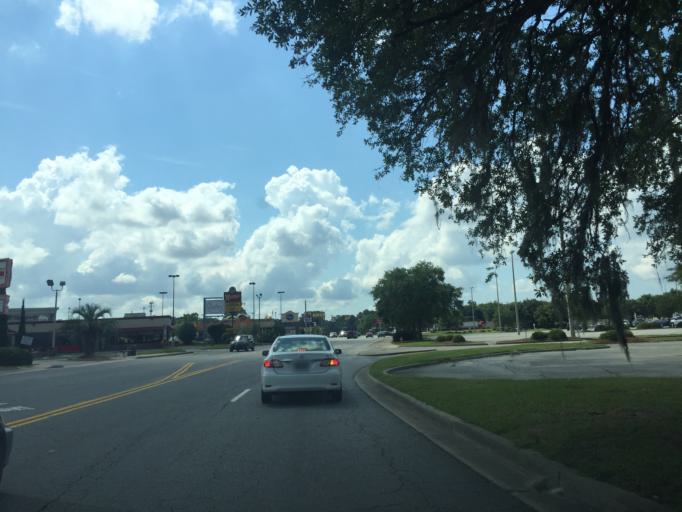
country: US
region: Georgia
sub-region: Chatham County
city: Isle of Hope
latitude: 32.0057
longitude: -81.1154
